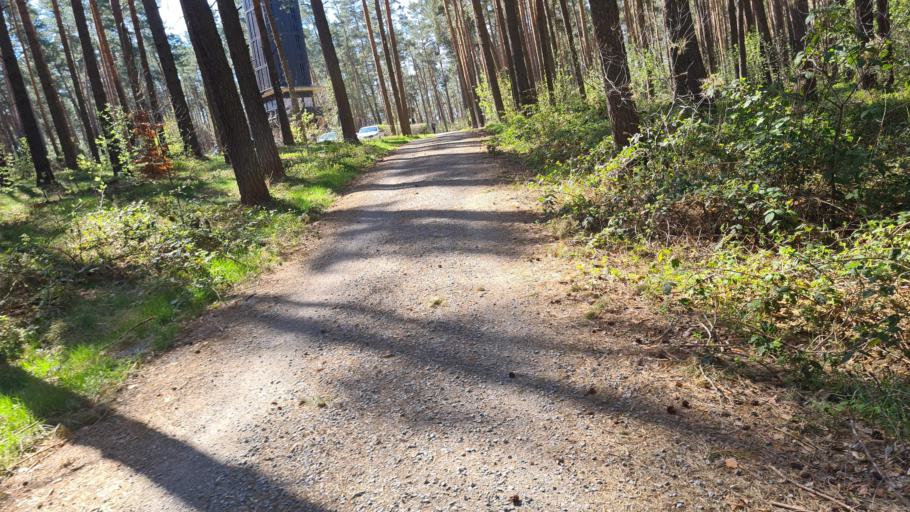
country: DE
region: Brandenburg
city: Groden
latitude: 51.3858
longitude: 13.5779
